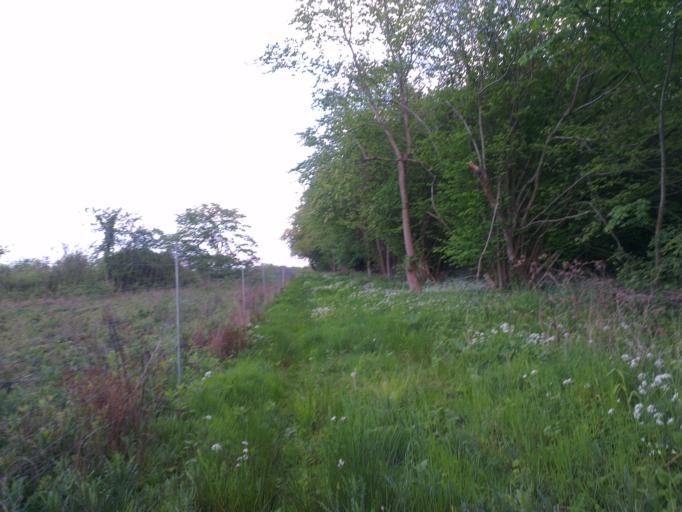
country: DK
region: Capital Region
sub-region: Frederikssund Kommune
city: Jaegerspris
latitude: 55.8550
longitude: 11.9609
